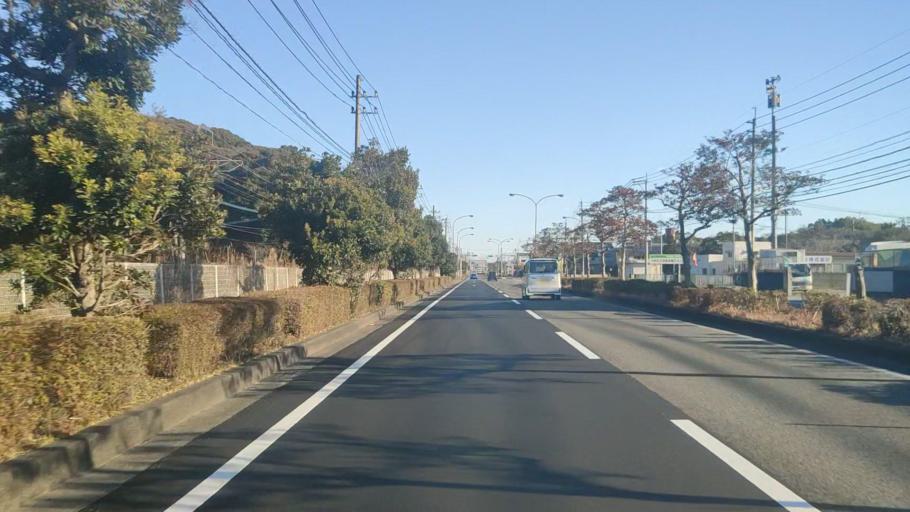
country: JP
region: Miyazaki
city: Nobeoka
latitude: 32.4524
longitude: 131.6413
